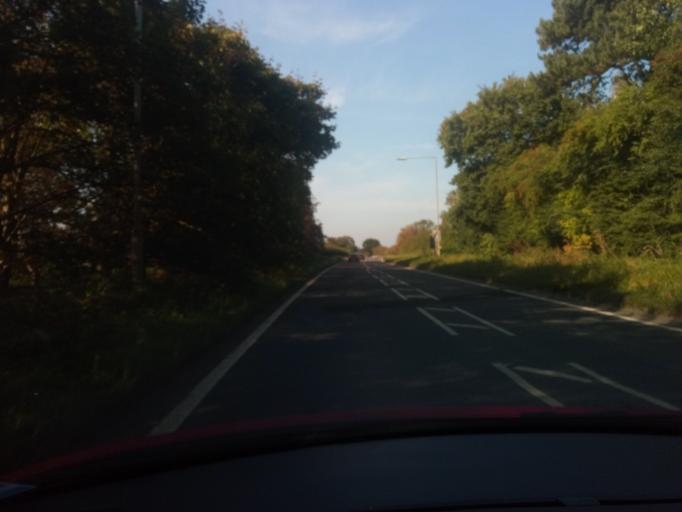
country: GB
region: England
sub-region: City of York
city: Skelton
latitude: 54.0181
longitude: -1.1571
